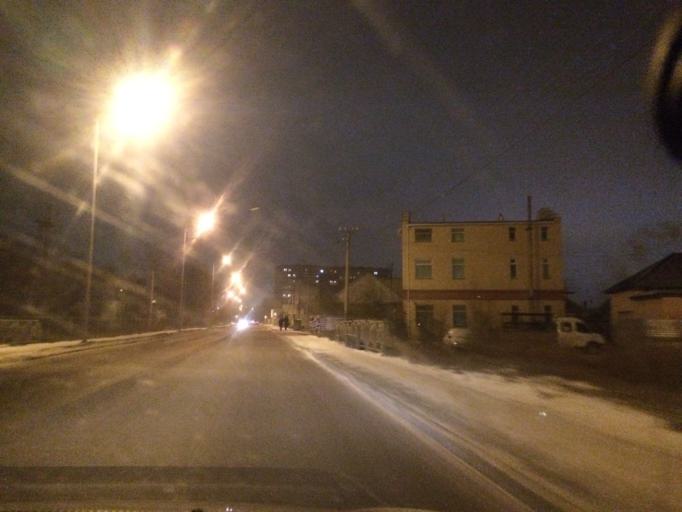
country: KZ
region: Astana Qalasy
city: Astana
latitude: 51.2037
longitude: 71.3825
